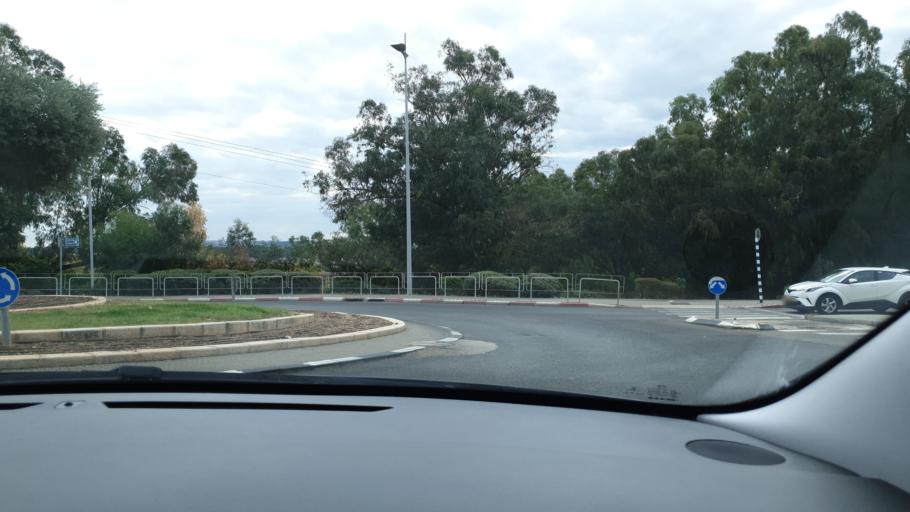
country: IL
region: Haifa
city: Qiryat Ata
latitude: 32.8073
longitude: 35.1172
